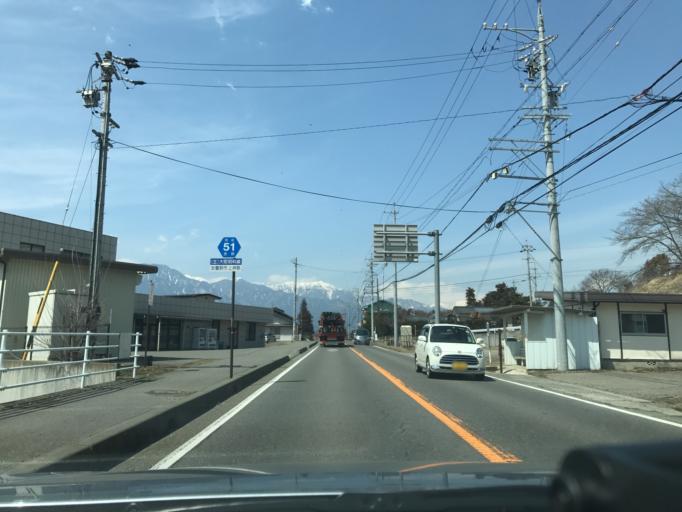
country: JP
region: Nagano
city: Hotaka
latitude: 36.3553
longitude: 137.9092
